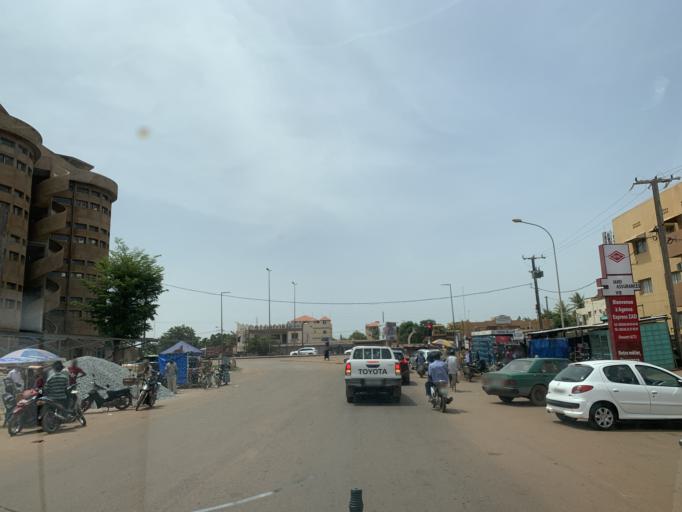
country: BF
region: Centre
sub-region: Kadiogo Province
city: Ouagadougou
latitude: 12.3361
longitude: -1.4996
